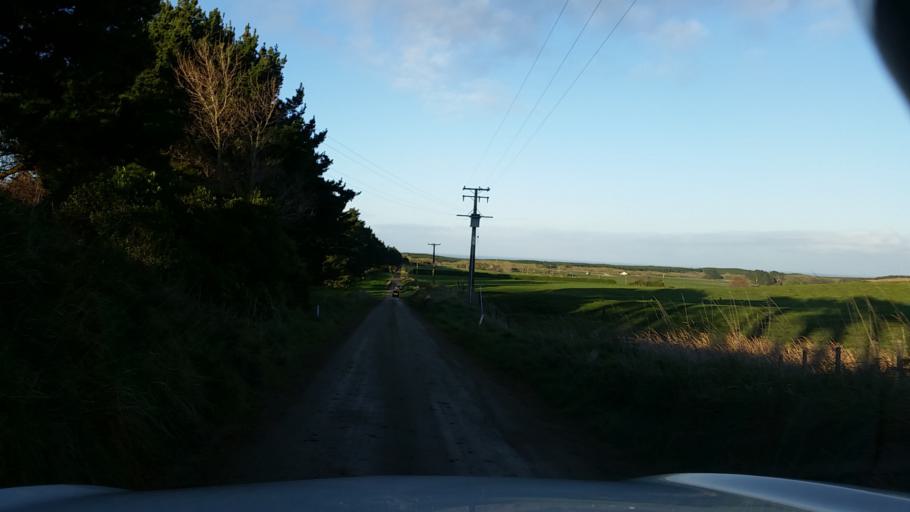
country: NZ
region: Manawatu-Wanganui
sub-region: Wanganui District
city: Wanganui
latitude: -39.8213
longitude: 174.7993
